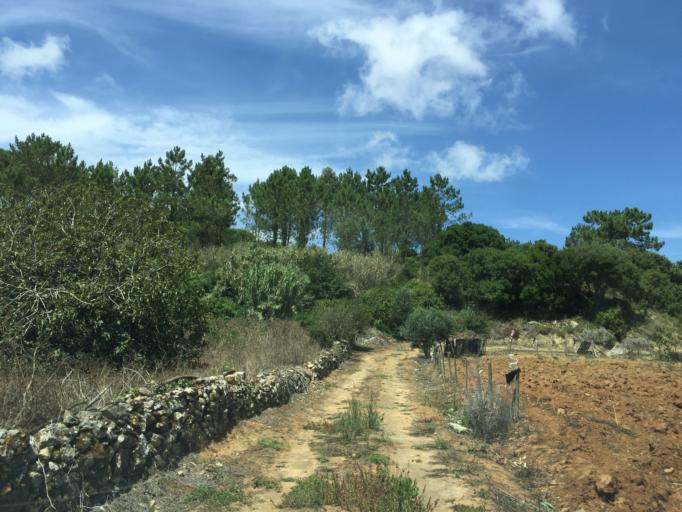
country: PT
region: Leiria
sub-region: Peniche
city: Atouguia da Baleia
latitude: 39.3251
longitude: -9.2674
